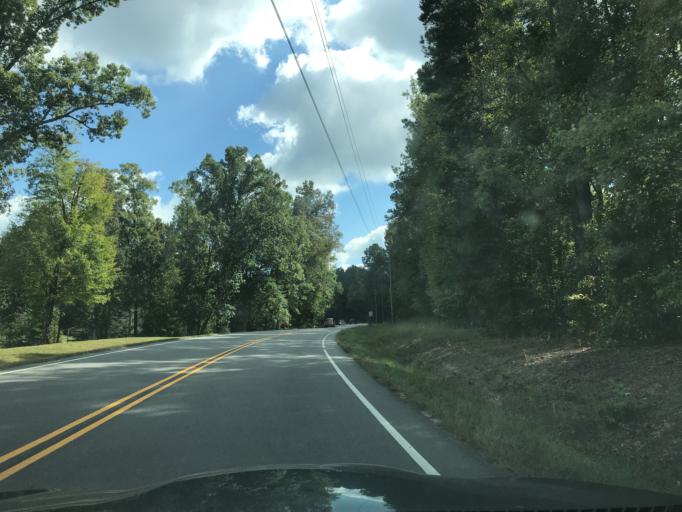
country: US
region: North Carolina
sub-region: Wake County
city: Wake Forest
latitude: 35.9279
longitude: -78.5270
